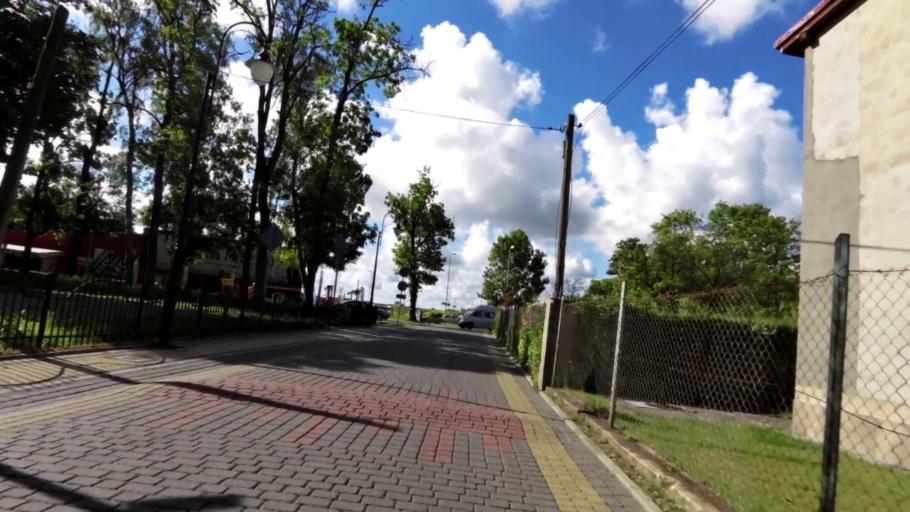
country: PL
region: West Pomeranian Voivodeship
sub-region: Powiat koszalinski
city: Mielno
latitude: 54.2617
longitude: 16.0684
